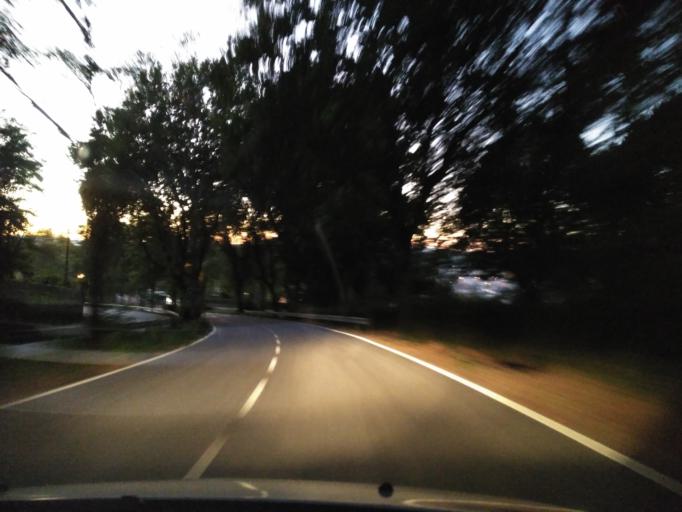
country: PT
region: Braga
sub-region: Braga
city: Adaufe
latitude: 41.5531
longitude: -8.3821
